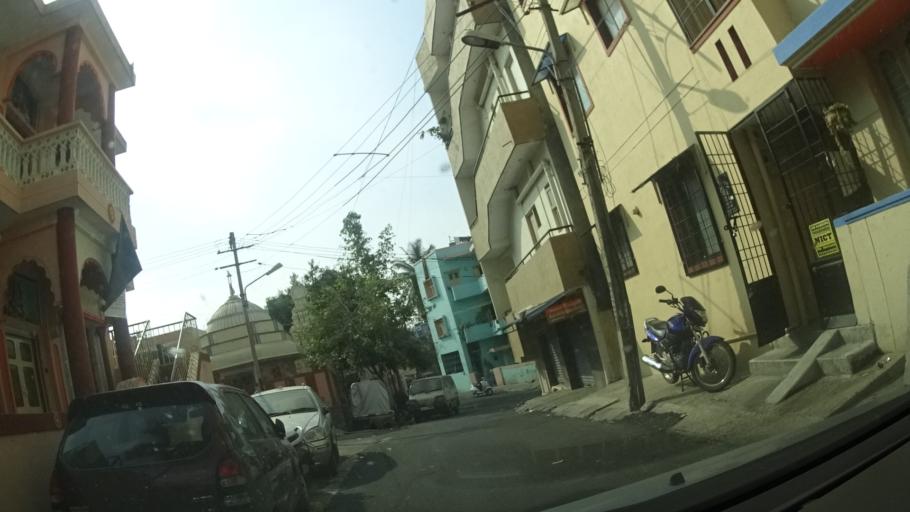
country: IN
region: Karnataka
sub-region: Bangalore Urban
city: Bangalore
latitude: 12.9457
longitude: 77.5595
